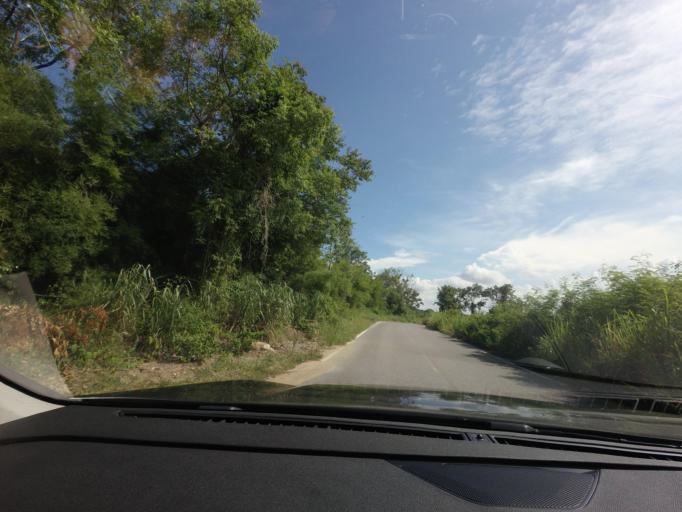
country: TH
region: Prachuap Khiri Khan
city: Hua Hin
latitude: 12.4893
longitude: 99.9425
